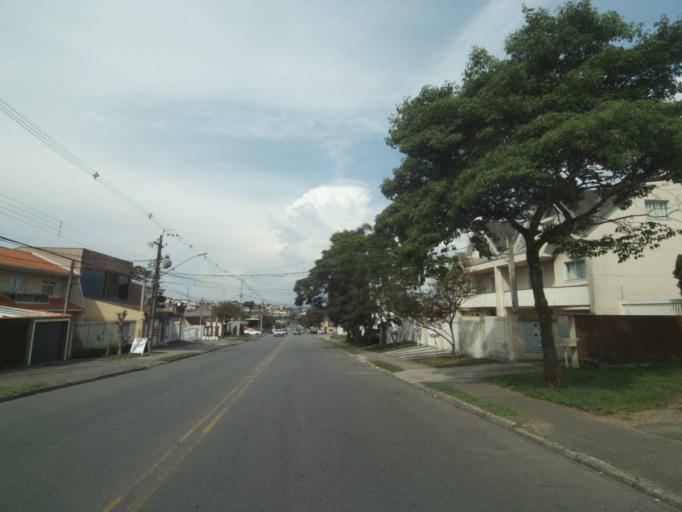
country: BR
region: Parana
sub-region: Pinhais
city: Pinhais
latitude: -25.4108
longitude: -49.2056
